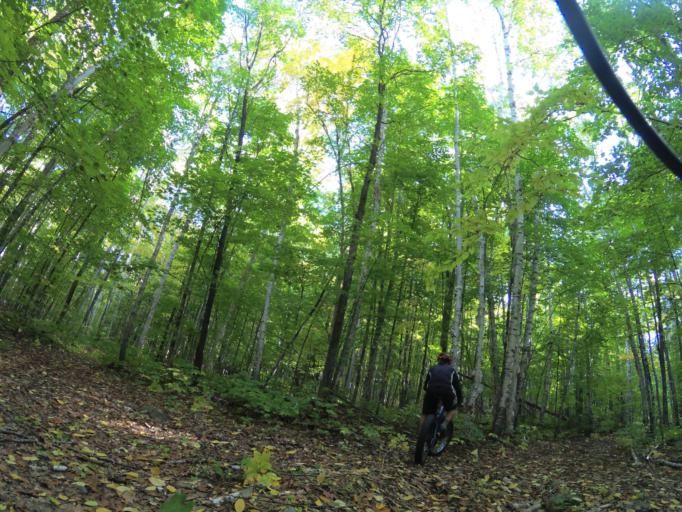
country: CA
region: Ontario
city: Pembroke
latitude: 45.3355
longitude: -77.1776
